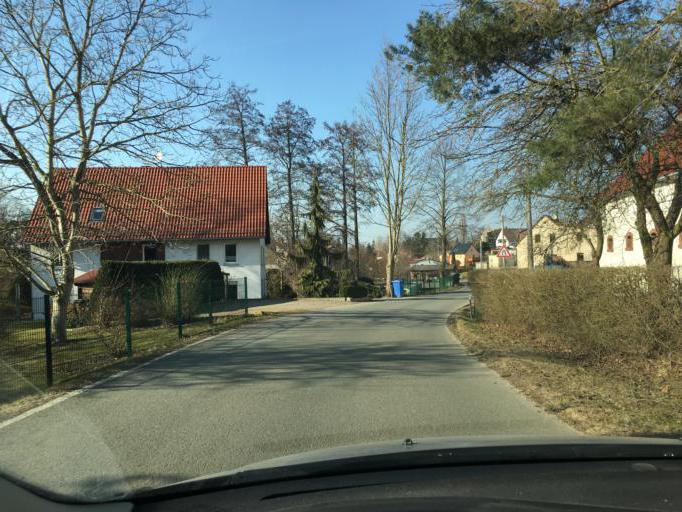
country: DE
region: Saxony
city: Waldenburg
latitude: 50.8931
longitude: 12.5820
